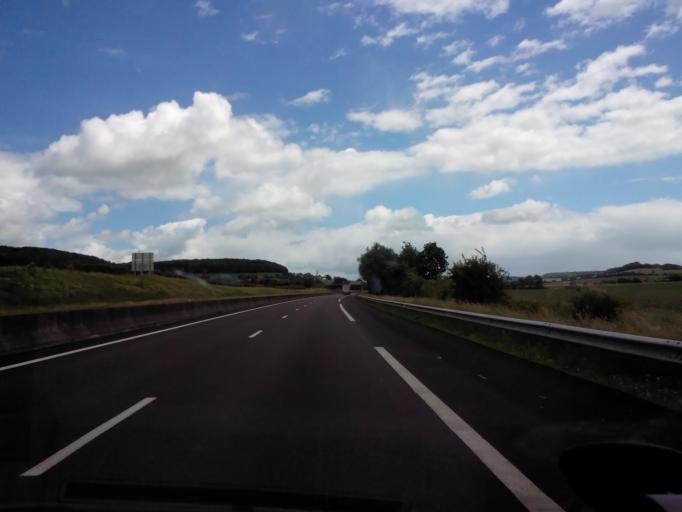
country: FR
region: Champagne-Ardenne
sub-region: Departement de la Haute-Marne
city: Rolampont
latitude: 47.9484
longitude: 5.3188
